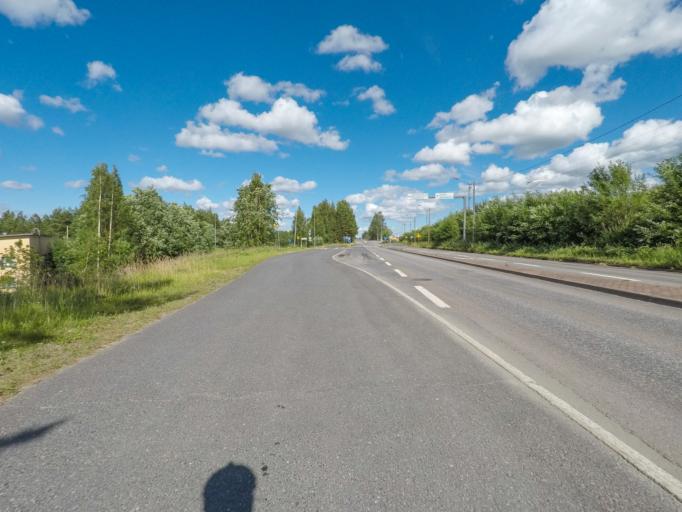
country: FI
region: South Karelia
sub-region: Lappeenranta
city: Lappeenranta
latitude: 61.0770
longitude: 28.2857
